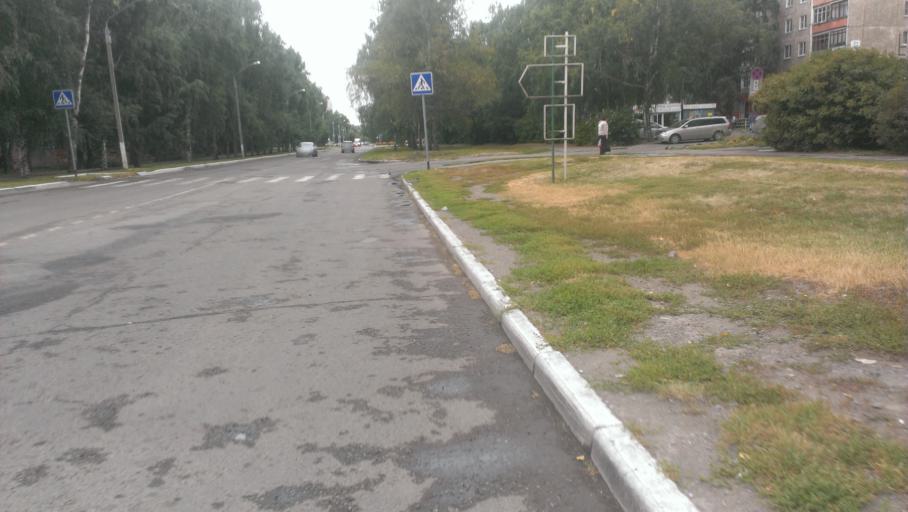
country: RU
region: Altai Krai
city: Novosilikatnyy
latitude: 53.3696
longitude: 83.6691
